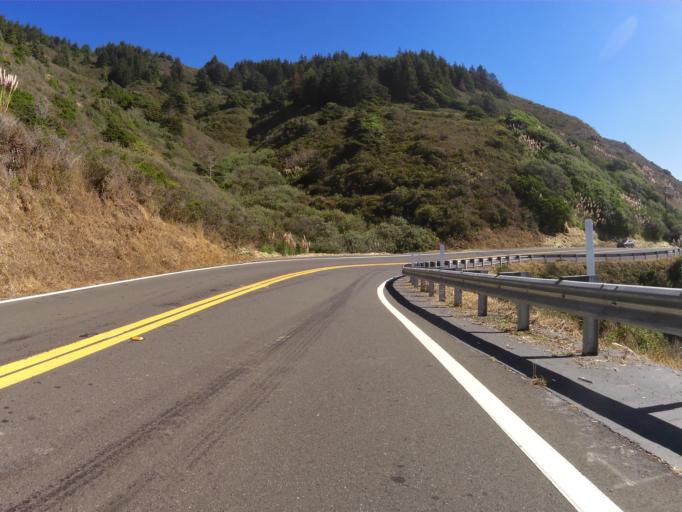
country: US
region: California
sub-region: Mendocino County
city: Fort Bragg
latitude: 39.6225
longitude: -123.7814
